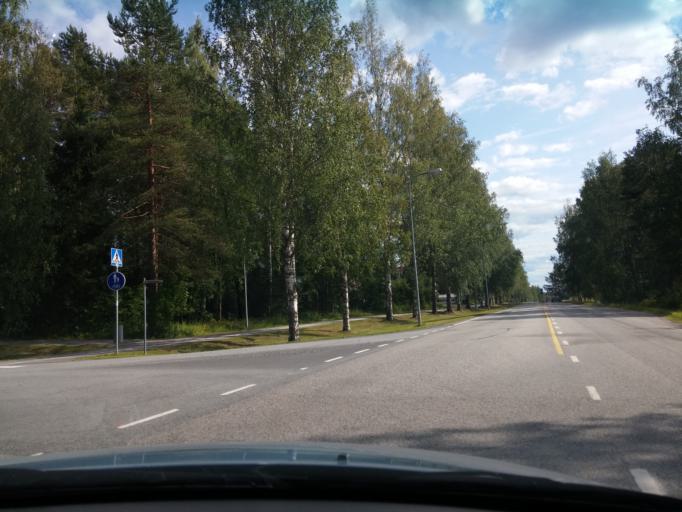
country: FI
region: Central Finland
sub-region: Keuruu
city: Keuruu
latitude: 62.2635
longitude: 24.6993
